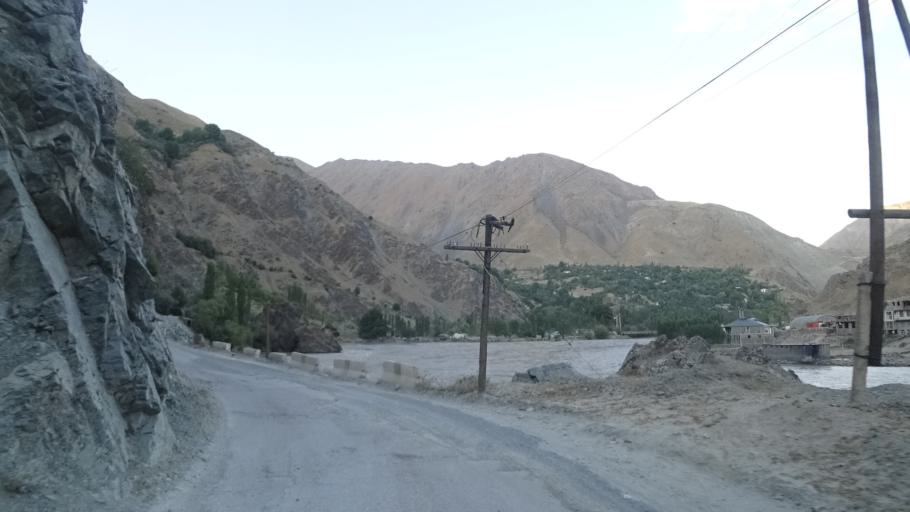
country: AF
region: Badakhshan
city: Nusay
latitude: 38.4522
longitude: 70.8220
